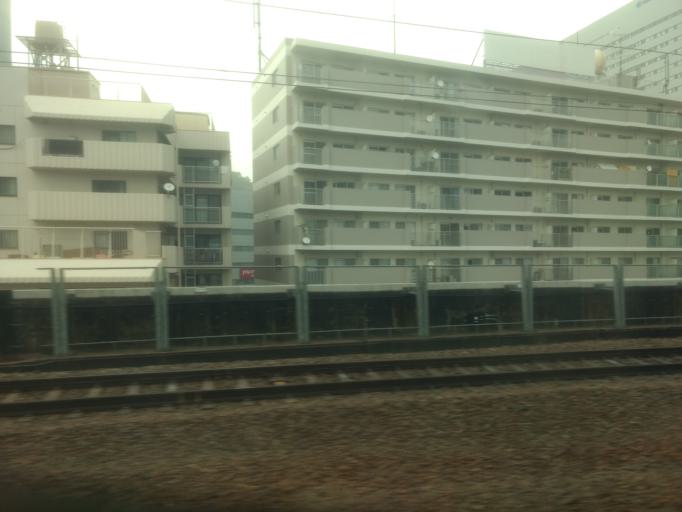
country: JP
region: Hiroshima
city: Hiroshima-shi
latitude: 34.4000
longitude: 132.4730
